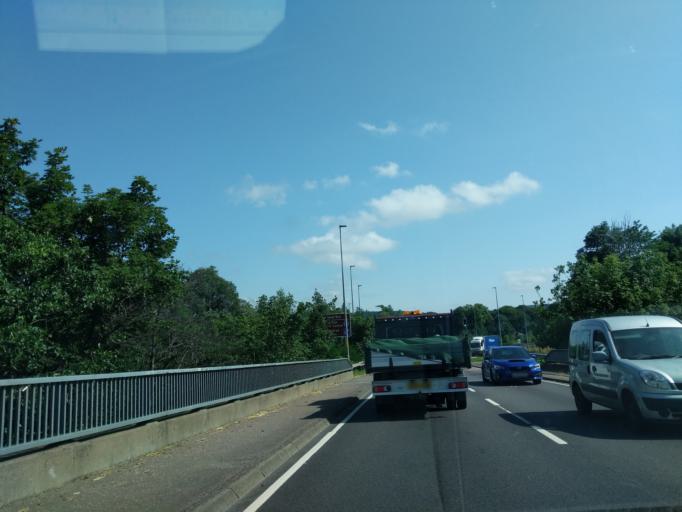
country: GB
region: Scotland
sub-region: Moray
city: Fochabers
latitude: 57.6201
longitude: -3.1054
